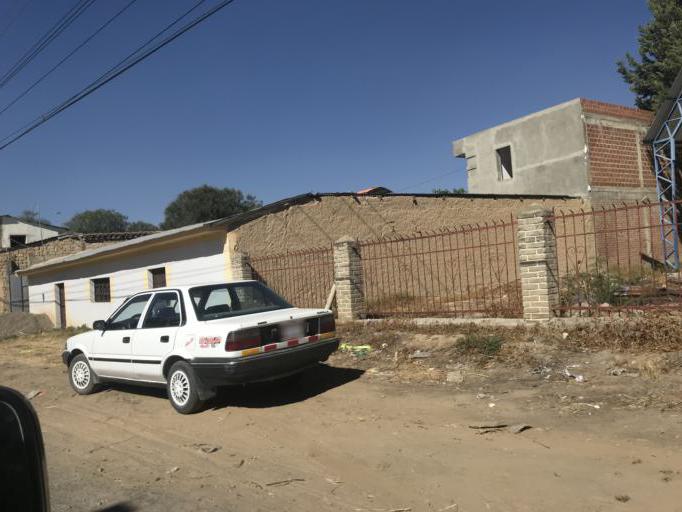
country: BO
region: Cochabamba
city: Punata
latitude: -17.5611
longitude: -65.8745
